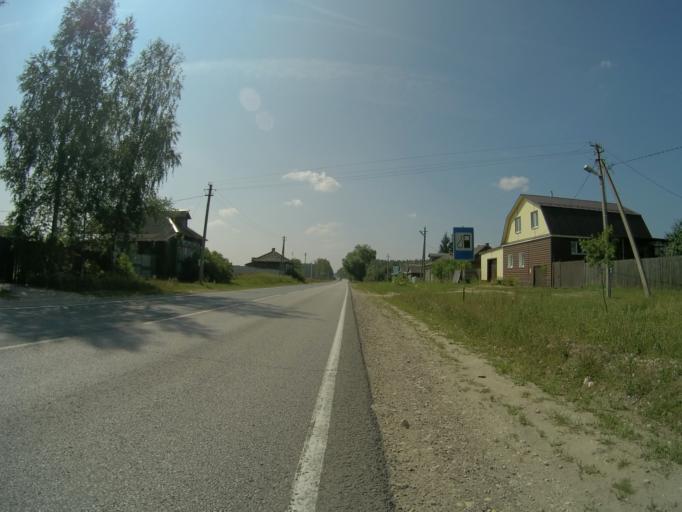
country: RU
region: Vladimir
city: Anopino
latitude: 55.6885
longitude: 40.7455
